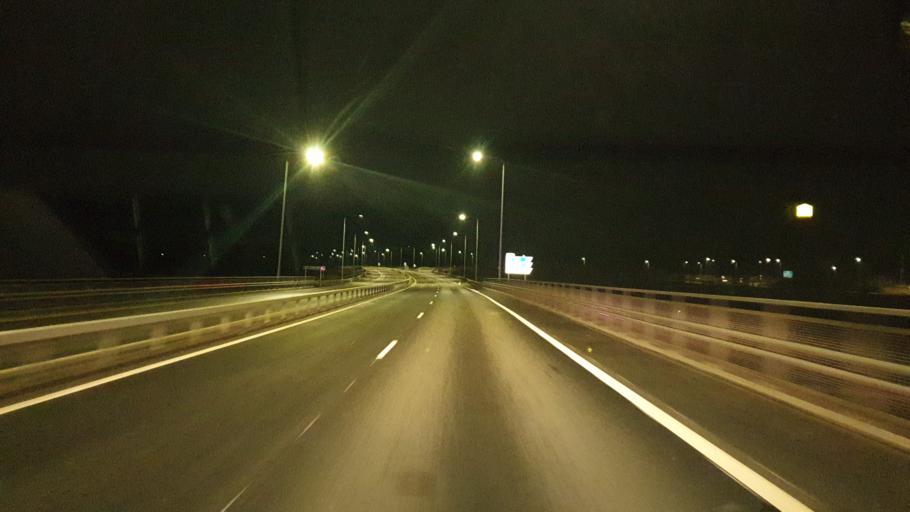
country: FI
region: Central Finland
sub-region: AEaenekoski
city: AEaenekoski
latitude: 62.6053
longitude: 25.6896
